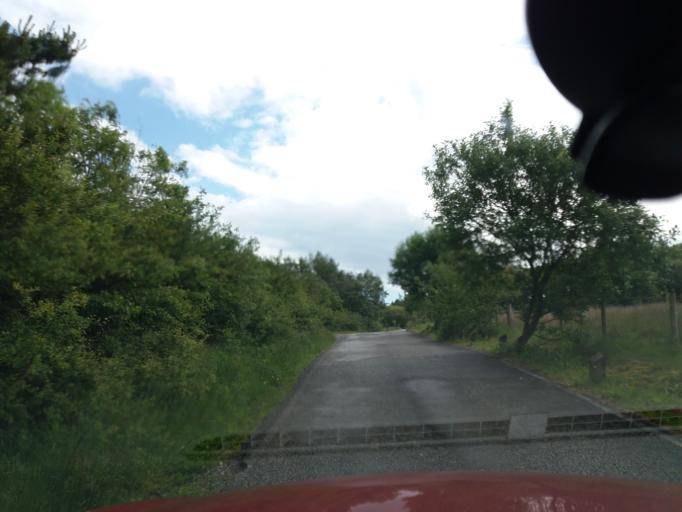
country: GB
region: England
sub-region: Blackburn with Darwen
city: Darwen
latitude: 53.6494
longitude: -2.4245
